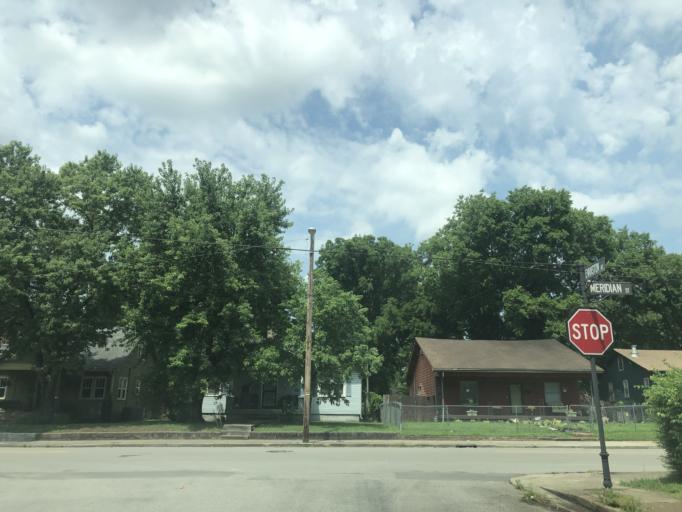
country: US
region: Tennessee
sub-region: Davidson County
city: Nashville
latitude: 36.1902
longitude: -86.7674
